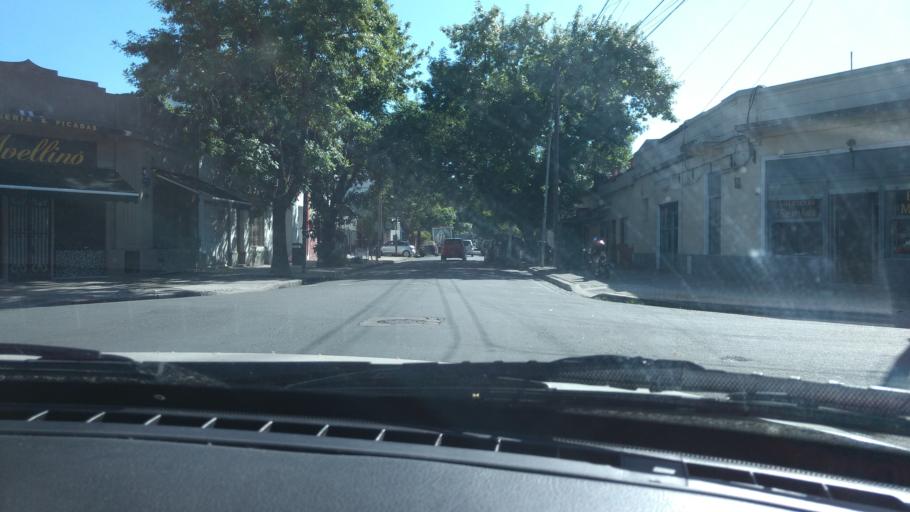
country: AR
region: Buenos Aires
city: Caseros
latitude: -34.6256
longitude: -58.5269
